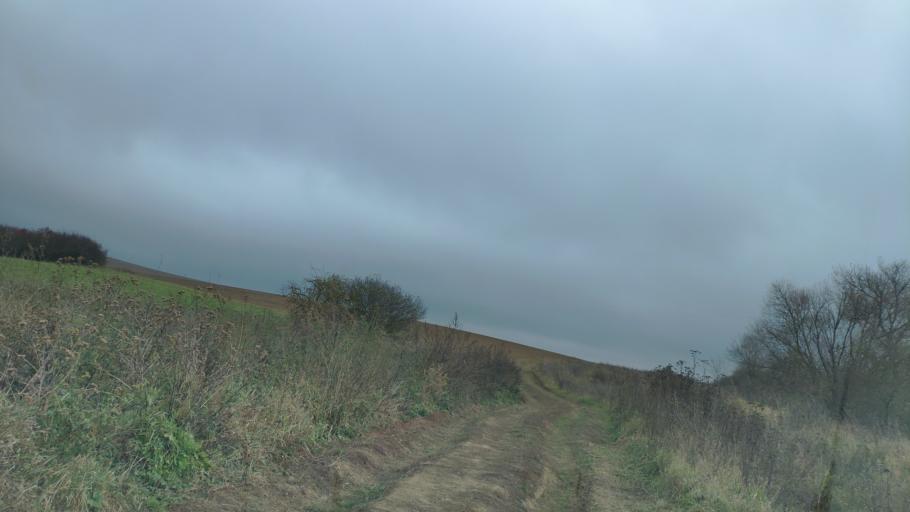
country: SK
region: Presovsky
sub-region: Okres Presov
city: Presov
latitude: 49.0178
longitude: 21.2012
